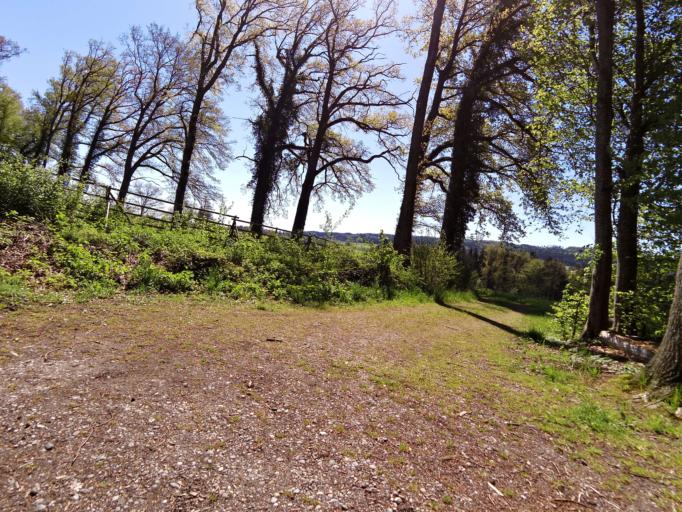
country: CH
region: Thurgau
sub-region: Weinfelden District
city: Berg
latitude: 47.6053
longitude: 9.1311
